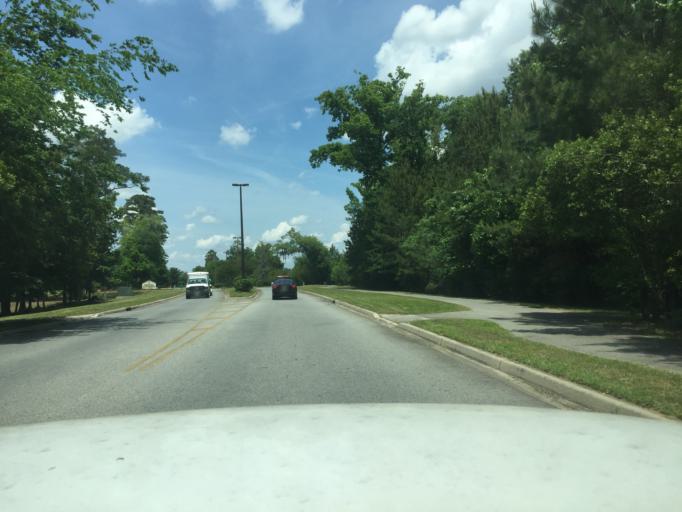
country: US
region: Georgia
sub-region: Chatham County
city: Georgetown
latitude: 32.0325
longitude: -81.2286
